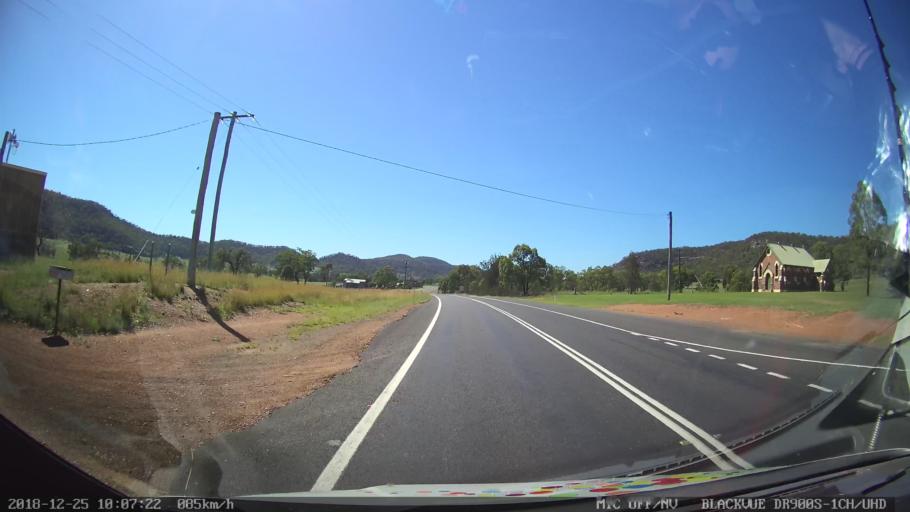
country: AU
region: New South Wales
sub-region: Upper Hunter Shire
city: Merriwa
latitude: -32.2704
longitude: 150.4976
